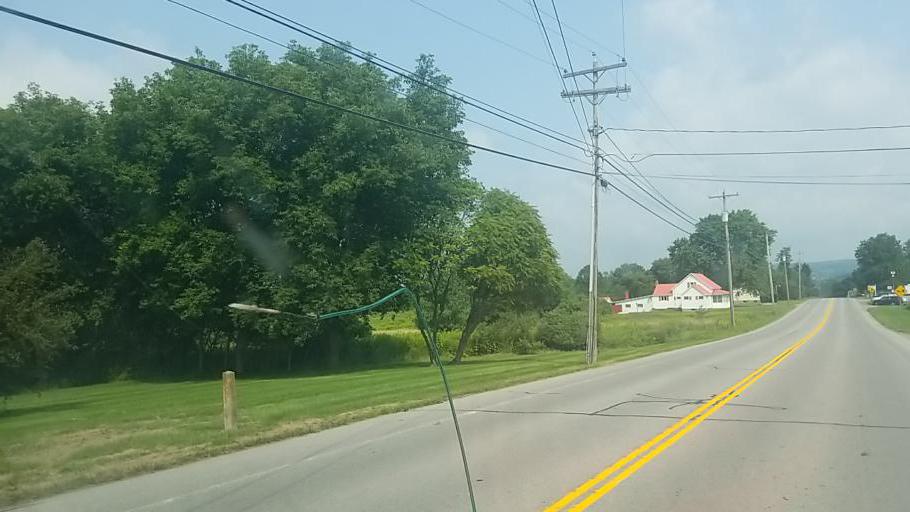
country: US
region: New York
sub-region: Montgomery County
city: Fort Plain
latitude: 42.9506
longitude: -74.6202
